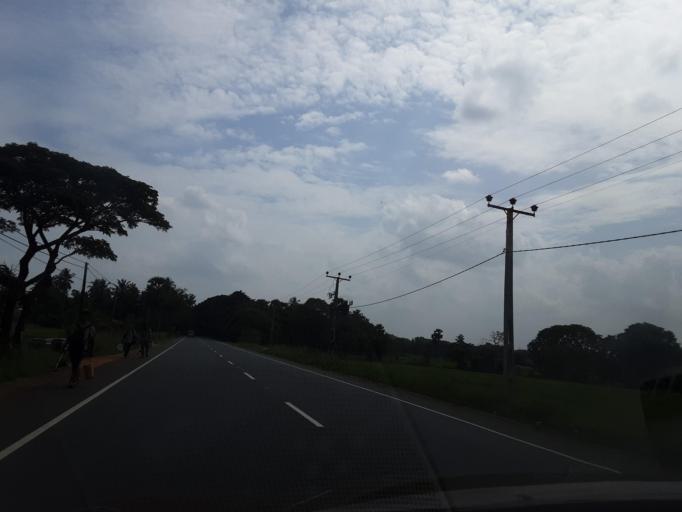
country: LK
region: North Central
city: Anuradhapura
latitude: 8.5161
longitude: 80.5031
